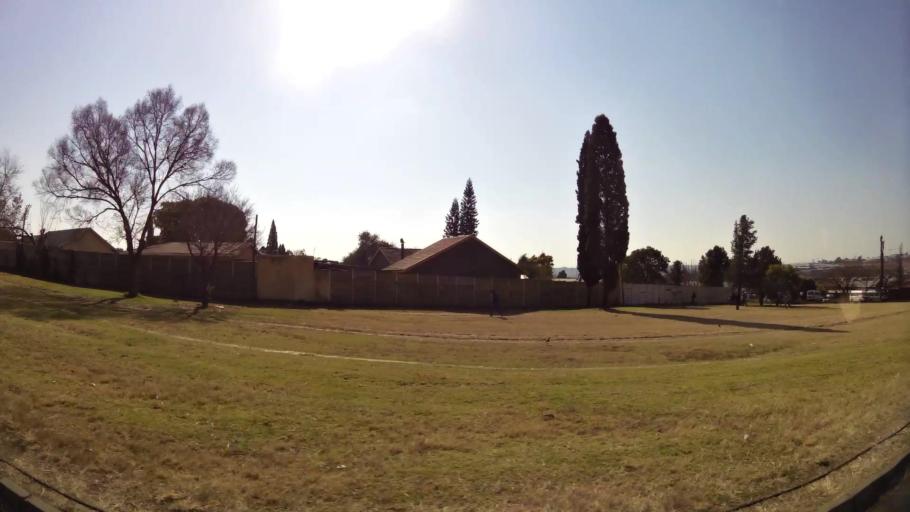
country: ZA
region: Gauteng
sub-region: City of Johannesburg Metropolitan Municipality
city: Modderfontein
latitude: -26.1246
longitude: 28.1723
